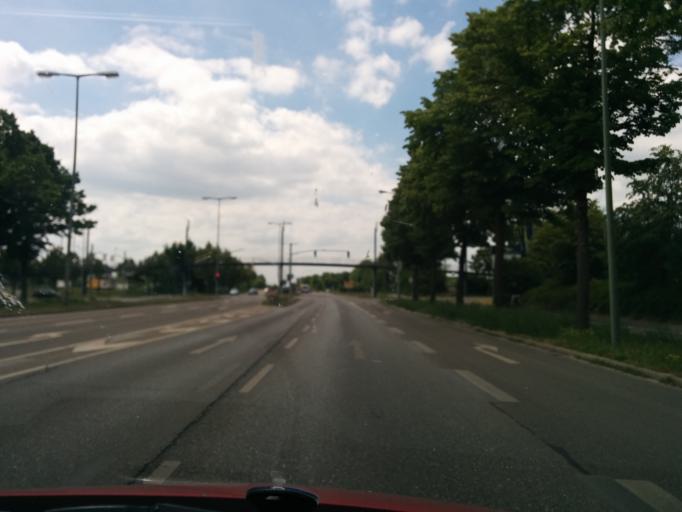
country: DE
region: Bavaria
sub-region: Swabia
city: Augsburg
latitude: 48.3379
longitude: 10.8954
